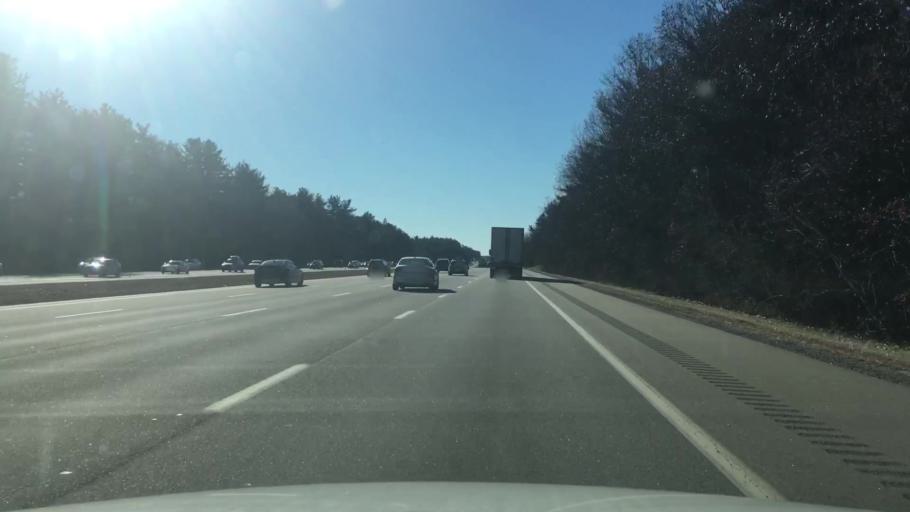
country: US
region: New Hampshire
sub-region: Rockingham County
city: Greenland
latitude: 43.0143
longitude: -70.8350
